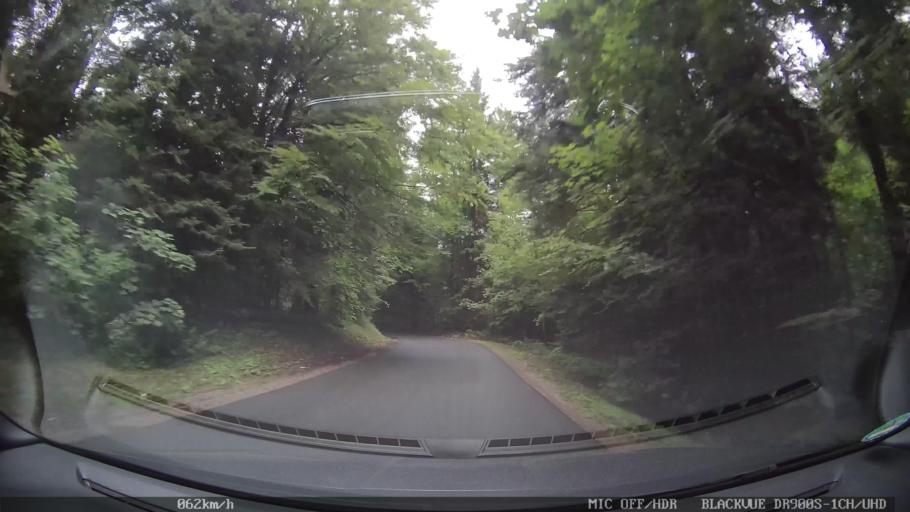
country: HR
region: Licko-Senjska
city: Jezerce
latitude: 44.9331
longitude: 15.5515
